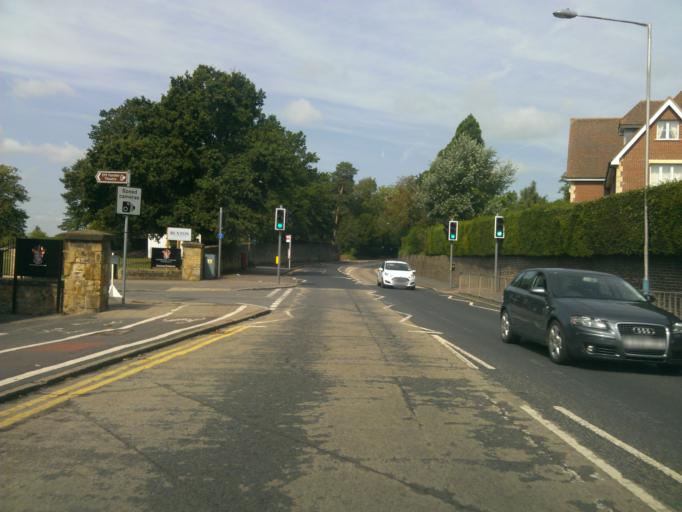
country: GB
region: England
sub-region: Kent
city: Tonbridge
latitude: 51.2021
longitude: 0.2756
